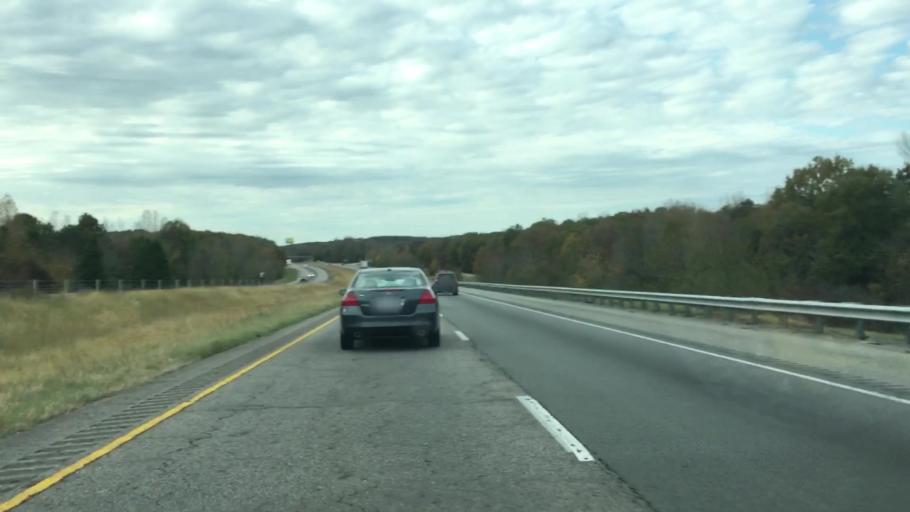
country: US
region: Arkansas
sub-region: Faulkner County
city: Conway
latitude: 35.1493
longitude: -92.5433
